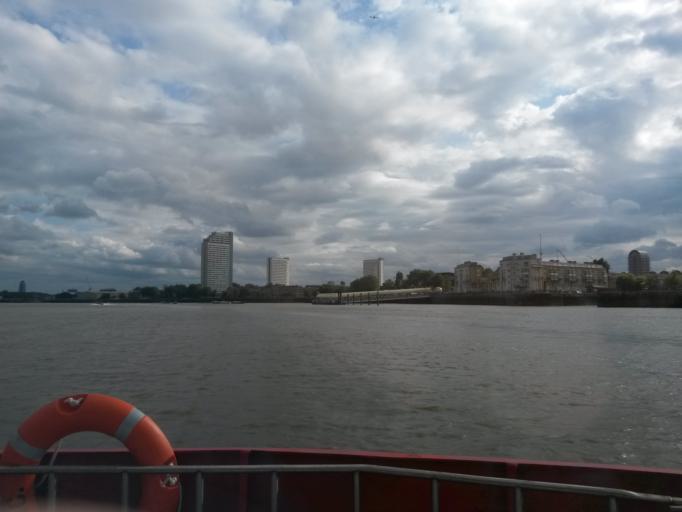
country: GB
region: England
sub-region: Greater London
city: Poplar
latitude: 51.4975
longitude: -0.0306
